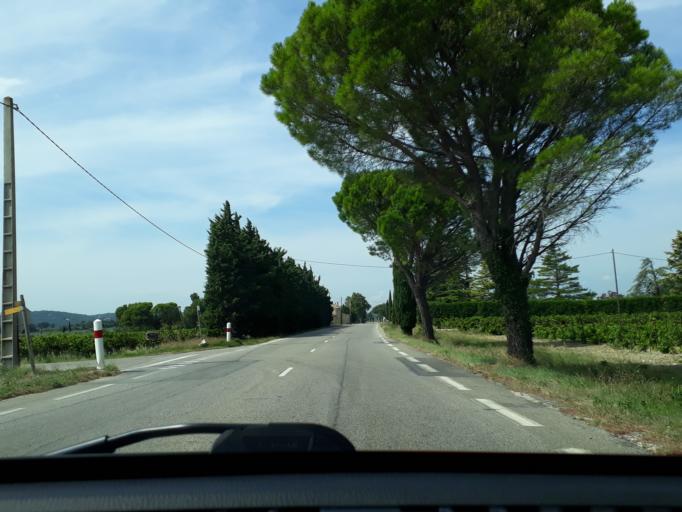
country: FR
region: Provence-Alpes-Cote d'Azur
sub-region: Departement du Vaucluse
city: Sainte-Cecile-les-Vignes
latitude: 44.2478
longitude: 4.8748
